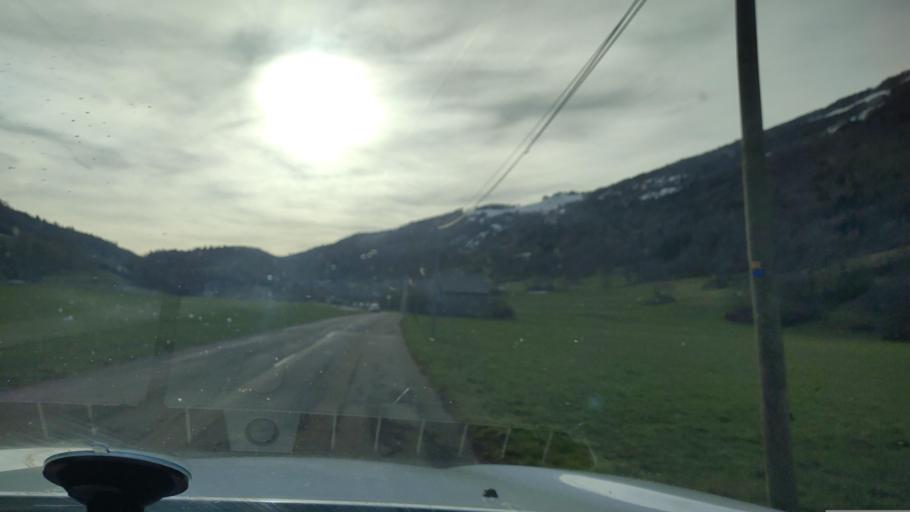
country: FR
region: Rhone-Alpes
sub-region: Departement de la Savoie
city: Coise-Saint-Jean-Pied-Gauthier
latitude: 45.6008
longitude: 6.1393
